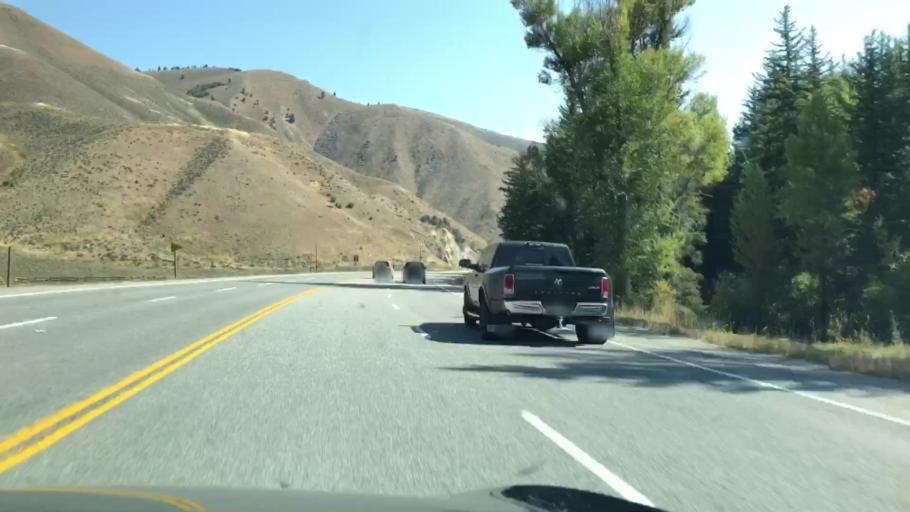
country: US
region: Wyoming
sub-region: Teton County
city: Hoback
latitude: 43.2982
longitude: -110.7868
